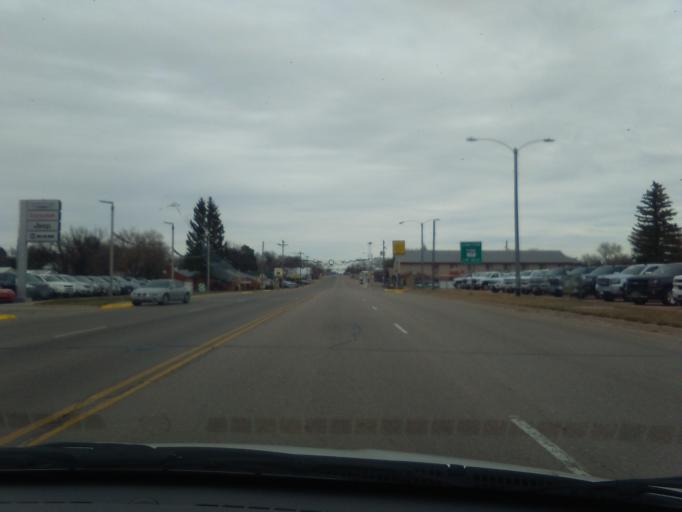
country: US
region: Colorado
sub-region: Yuma County
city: Yuma
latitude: 40.1184
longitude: -102.7307
